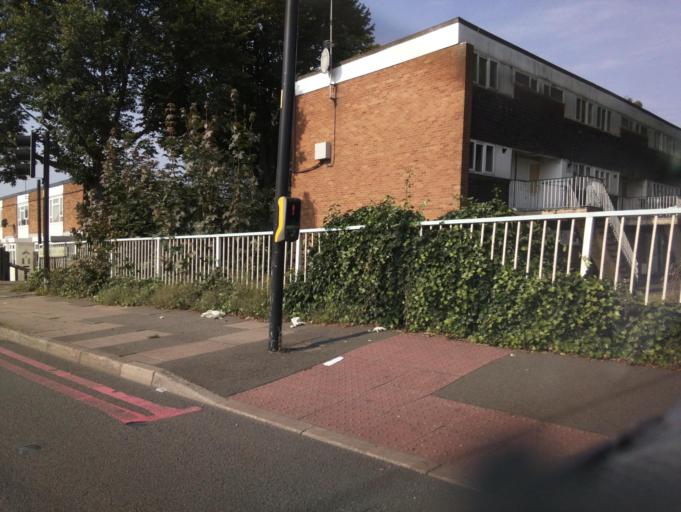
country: GB
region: England
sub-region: Sandwell
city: West Bromwich
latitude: 52.5310
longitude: -1.9883
